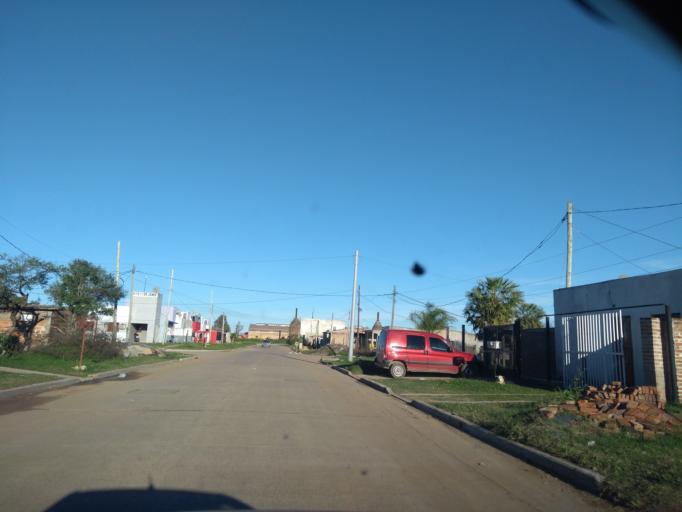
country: AR
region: Chaco
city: Barranqueras
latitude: -27.4929
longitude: -58.9354
